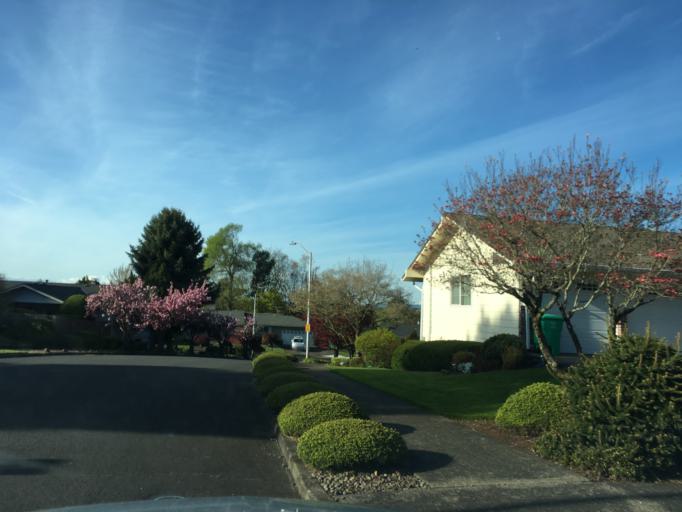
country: US
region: Oregon
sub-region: Multnomah County
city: Lents
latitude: 45.5495
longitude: -122.5209
